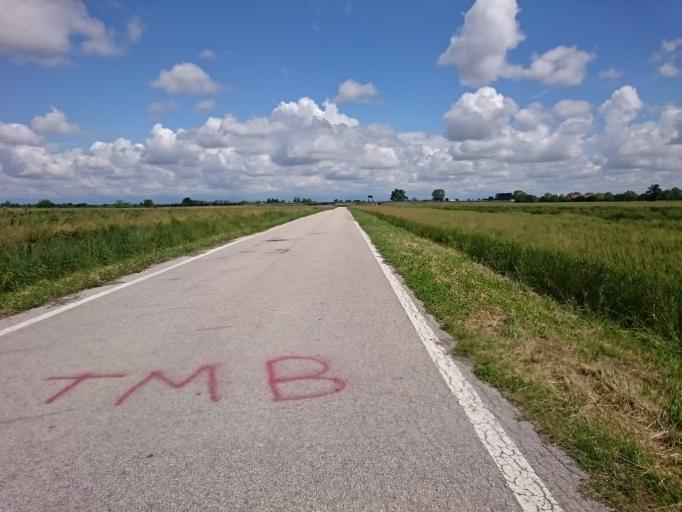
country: IT
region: Veneto
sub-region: Provincia di Padova
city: Arlesega
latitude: 45.4666
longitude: 11.7258
